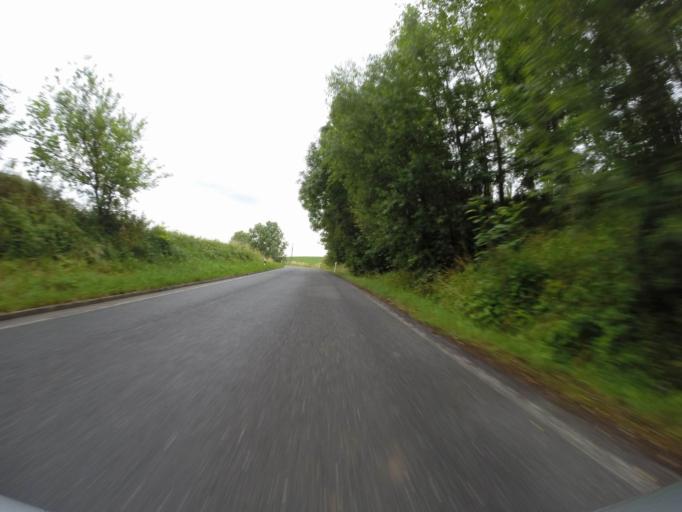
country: DE
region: Thuringia
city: Nausnitz
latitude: 50.9550
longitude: 11.7195
